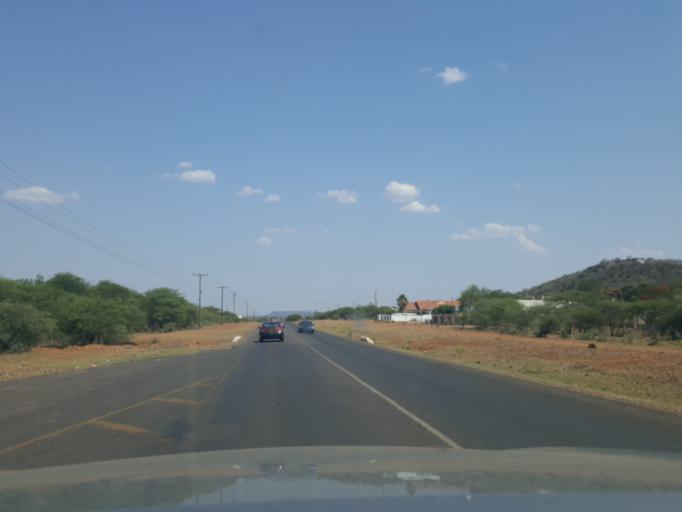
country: BW
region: South East
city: Ramotswa
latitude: -24.8345
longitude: 25.8162
